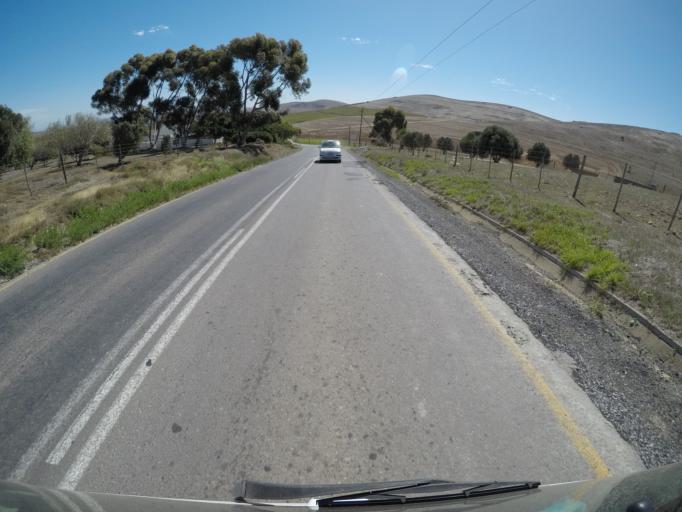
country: ZA
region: Western Cape
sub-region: City of Cape Town
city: Kraaifontein
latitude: -33.7940
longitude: 18.6049
